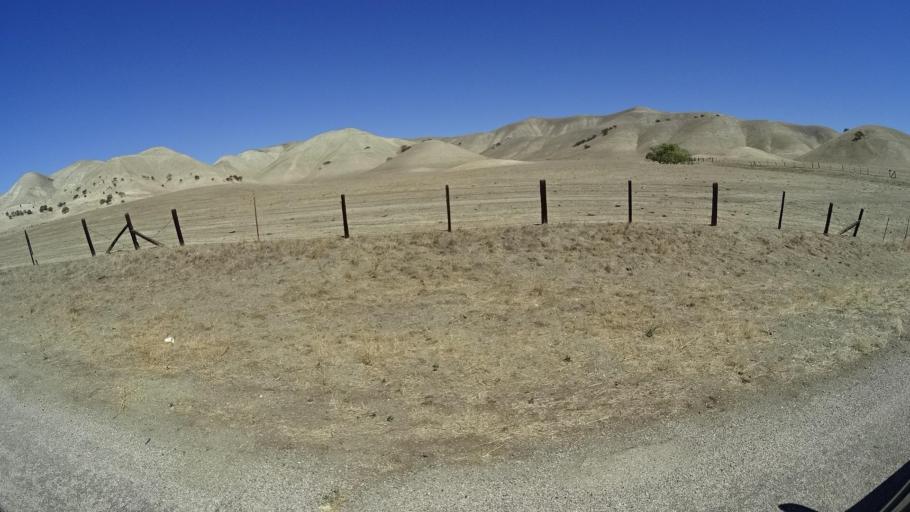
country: US
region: California
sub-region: Monterey County
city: King City
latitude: 36.2897
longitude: -120.9679
